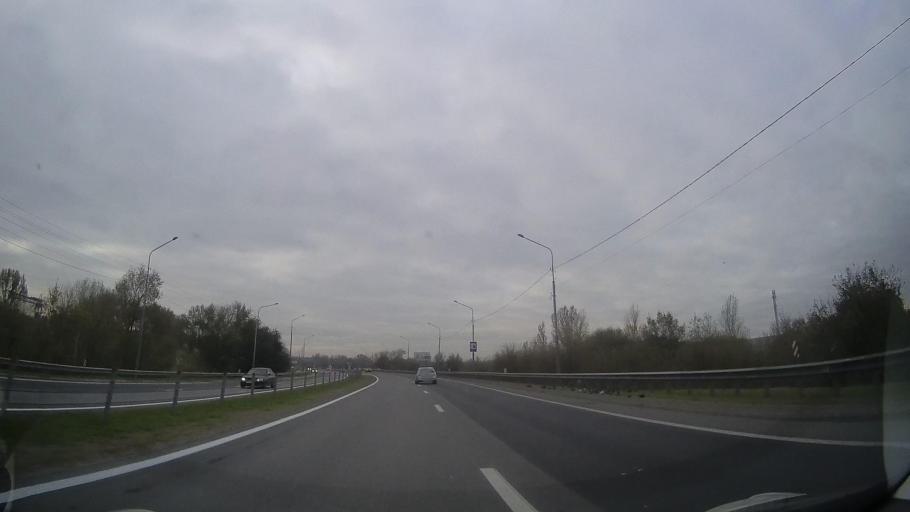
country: RU
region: Rostov
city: Bataysk
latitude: 47.0997
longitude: 39.7632
